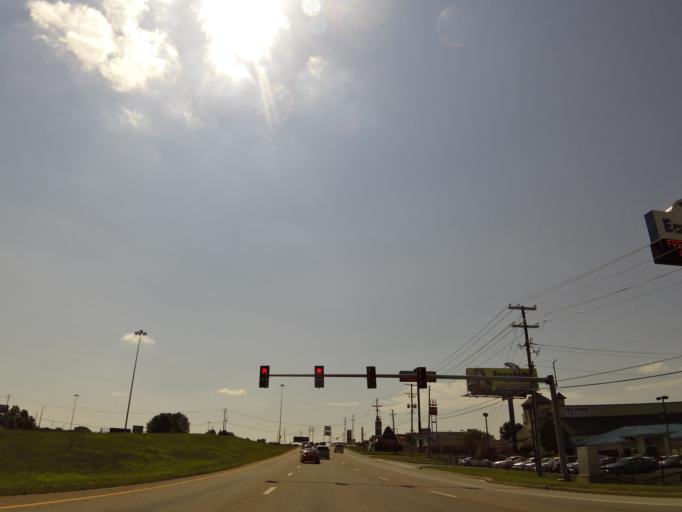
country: US
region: Tennessee
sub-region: Knox County
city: Farragut
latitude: 35.9248
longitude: -84.0629
